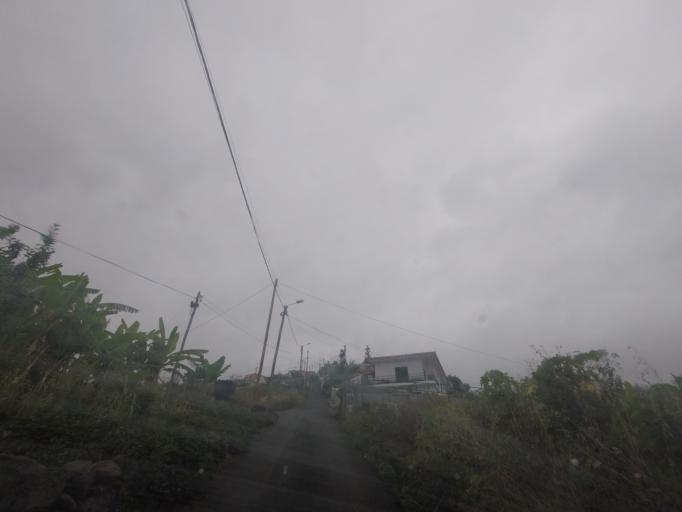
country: PT
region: Madeira
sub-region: Funchal
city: Nossa Senhora do Monte
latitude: 32.6673
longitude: -16.8999
